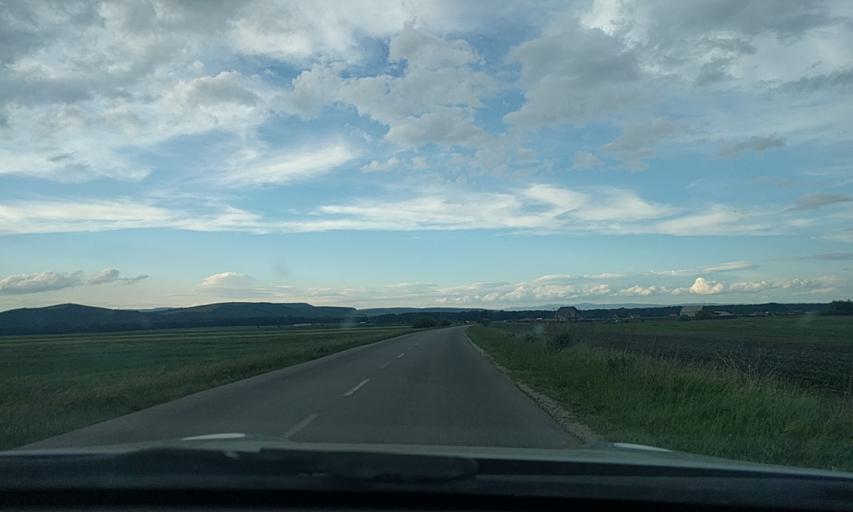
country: RO
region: Brasov
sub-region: Comuna Harman
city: Harman
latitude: 45.7314
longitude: 25.7006
